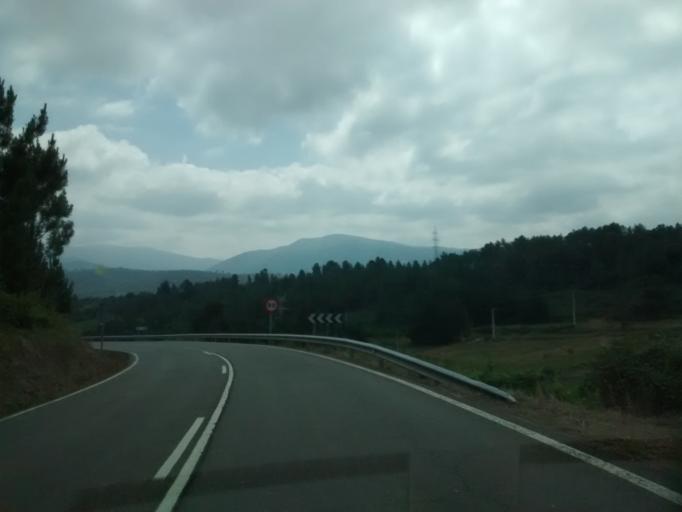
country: ES
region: Galicia
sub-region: Provincia de Ourense
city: Petin
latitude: 42.3493
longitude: -7.1569
